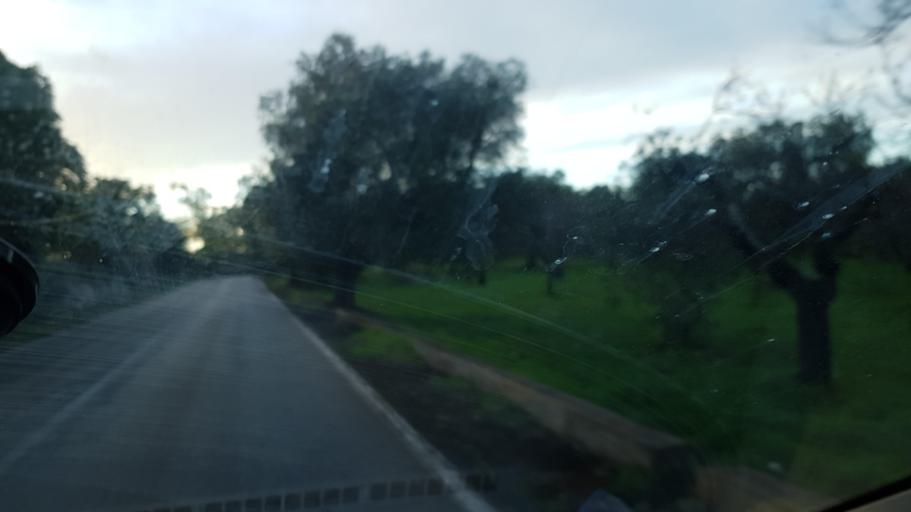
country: IT
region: Apulia
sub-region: Provincia di Brindisi
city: San Michele Salentino
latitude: 40.6427
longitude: 17.5973
